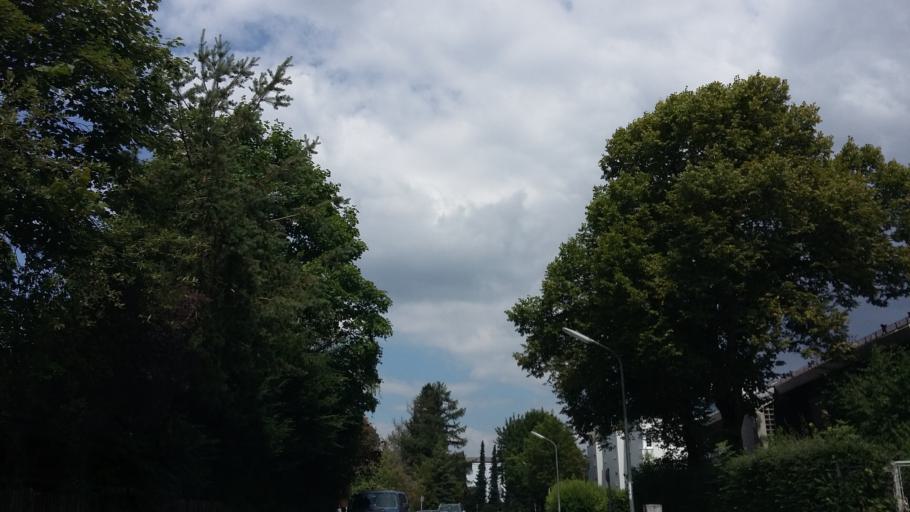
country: DE
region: Bavaria
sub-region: Upper Bavaria
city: Planegg
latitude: 48.0910
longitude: 11.4116
